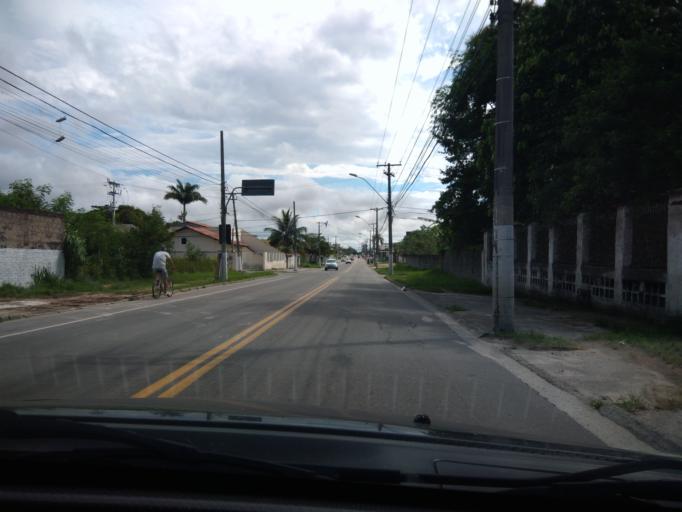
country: BR
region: Rio de Janeiro
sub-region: Niteroi
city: Niteroi
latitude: -22.9257
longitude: -43.0095
